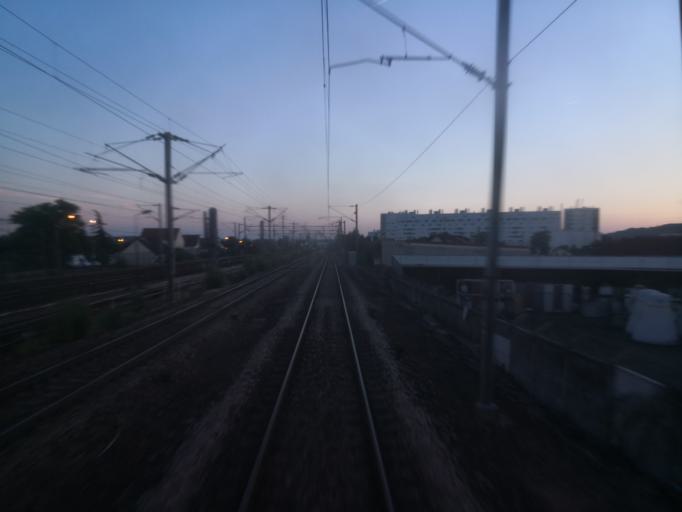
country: FR
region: Ile-de-France
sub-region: Departement des Yvelines
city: Les Mureaux
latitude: 48.9946
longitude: 1.9195
